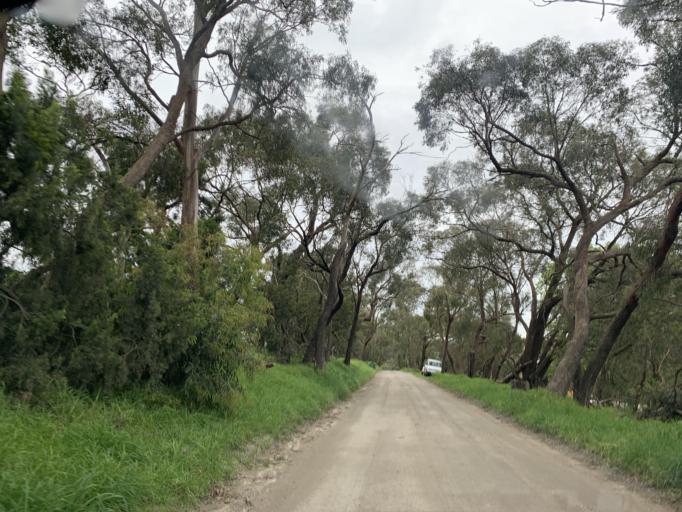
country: AU
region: Victoria
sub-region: Cardinia
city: Garfield
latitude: -38.0994
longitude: 145.6459
